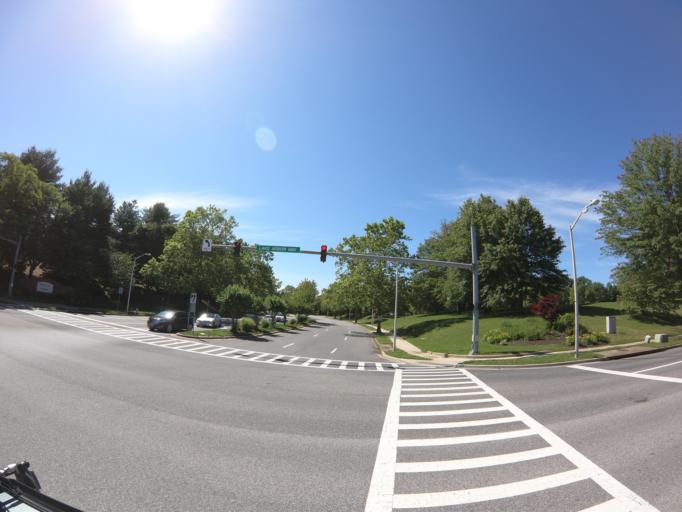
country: US
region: Maryland
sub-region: Prince George's County
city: Lake Arbor
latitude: 38.9060
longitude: -76.8275
